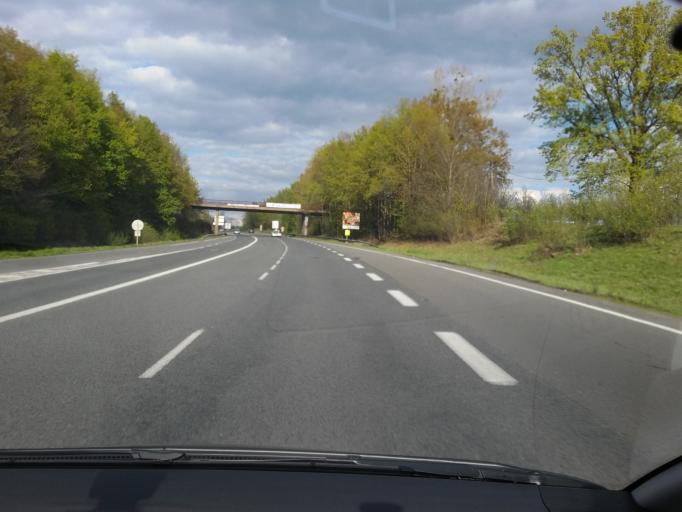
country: FR
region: Picardie
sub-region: Departement de l'Oise
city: Remy
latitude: 49.4007
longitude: 2.7029
